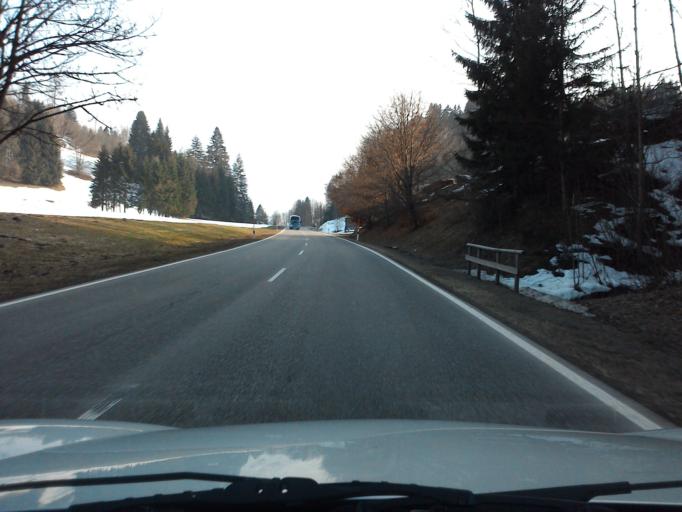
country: DE
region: Bavaria
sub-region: Swabia
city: Oberstdorf
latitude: 47.4203
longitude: 10.2636
